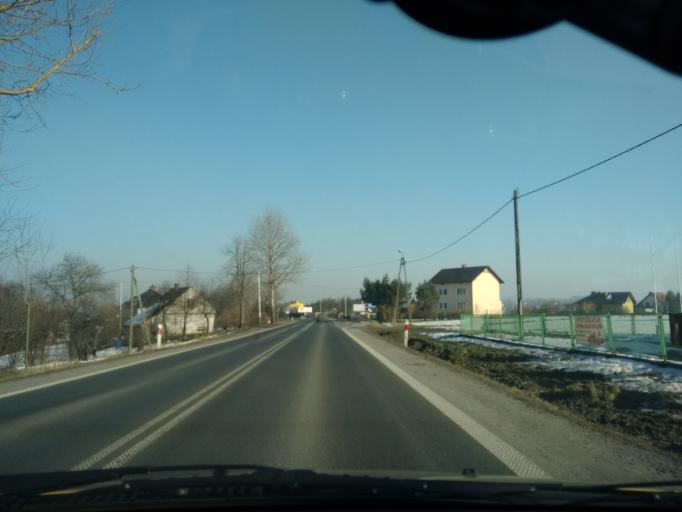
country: PL
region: Lesser Poland Voivodeship
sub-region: Powiat wadowicki
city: Chocznia
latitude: 49.8693
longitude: 19.4395
